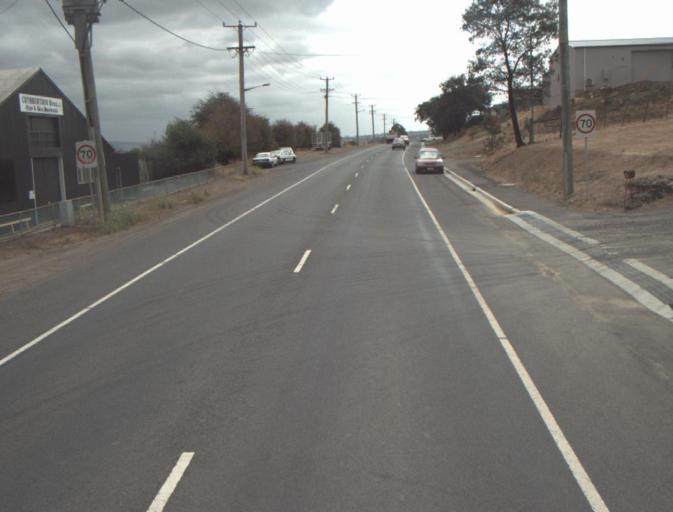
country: AU
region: Tasmania
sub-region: Launceston
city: Newstead
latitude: -41.4441
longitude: 147.1829
